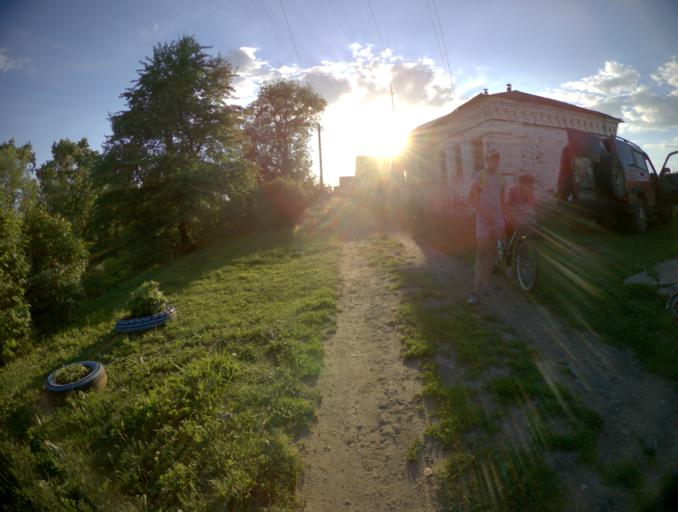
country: RU
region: Vladimir
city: Stavrovo
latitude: 56.2928
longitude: 39.9501
